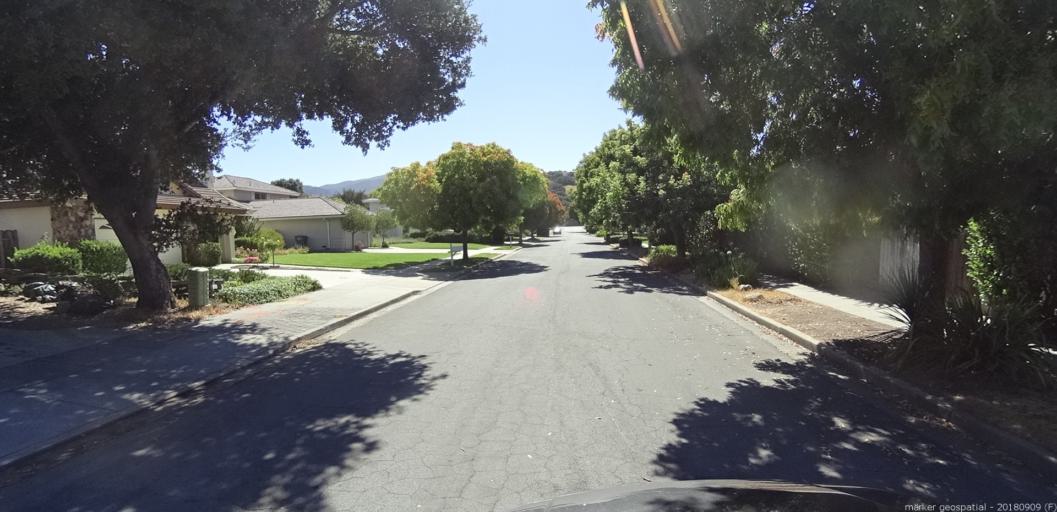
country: US
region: California
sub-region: Monterey County
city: Salinas
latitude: 36.5957
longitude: -121.7070
